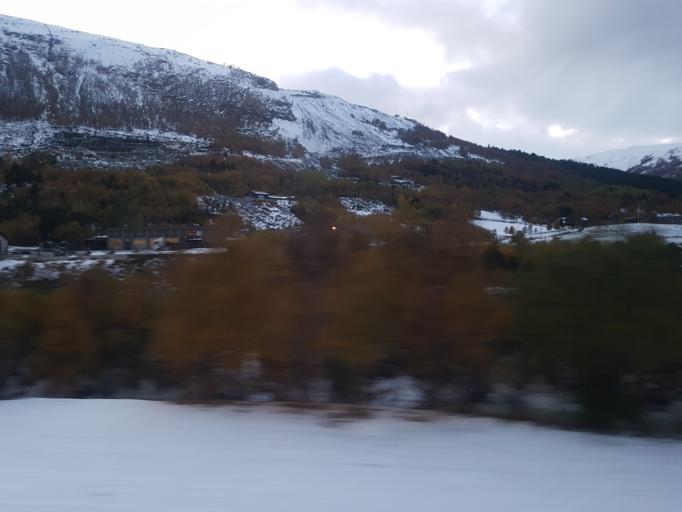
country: NO
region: Sor-Trondelag
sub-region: Oppdal
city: Oppdal
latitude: 62.4301
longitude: 9.6098
